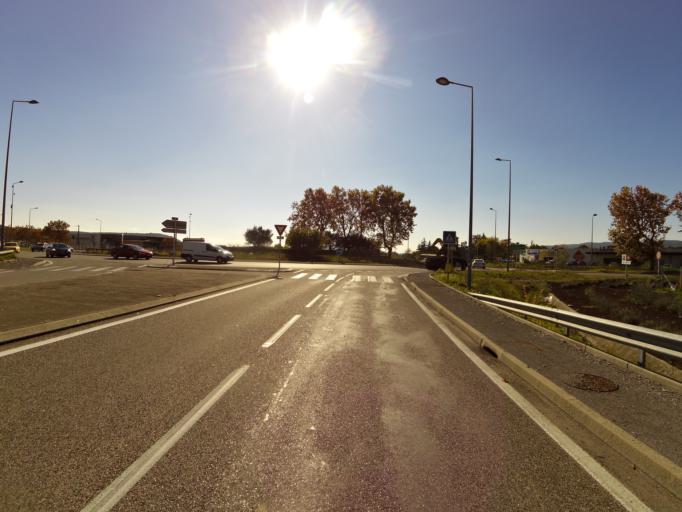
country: FR
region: Rhone-Alpes
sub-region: Departement de l'Ardeche
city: Saint-Privat
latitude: 44.6135
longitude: 4.4082
